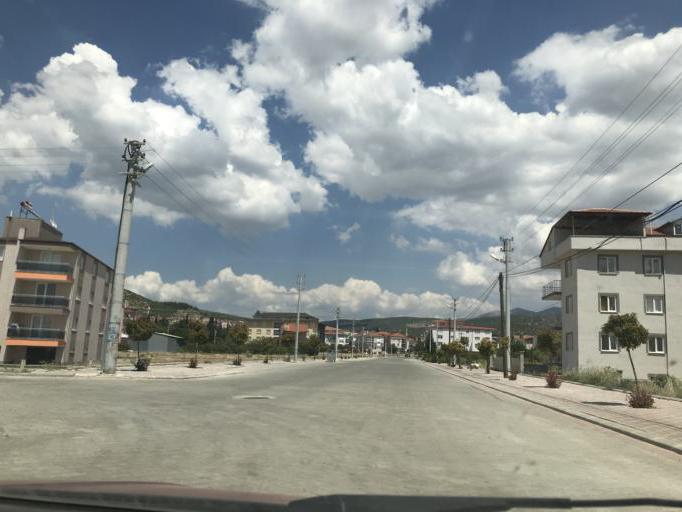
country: TR
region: Denizli
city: Tavas
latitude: 37.5707
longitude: 29.0605
